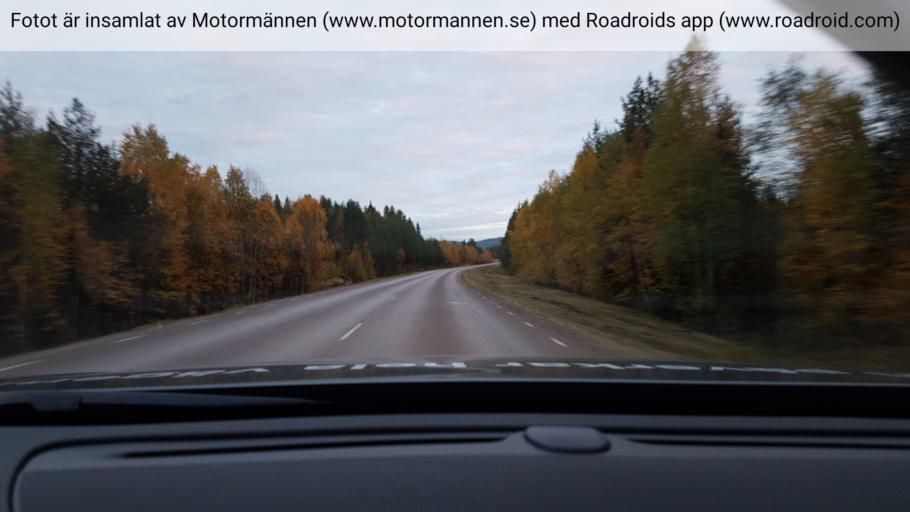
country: SE
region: Norrbotten
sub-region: Alvsbyns Kommun
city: AElvsbyn
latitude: 65.8891
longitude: 20.3494
